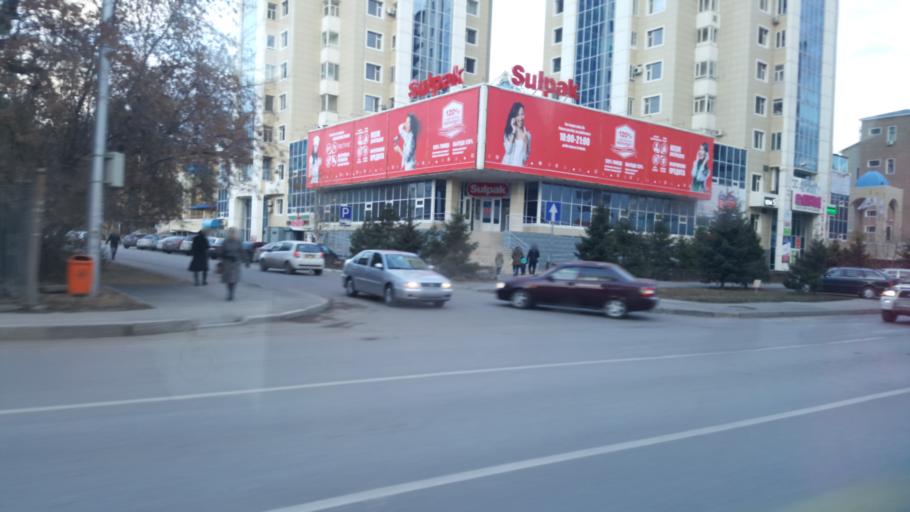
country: KZ
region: Astana Qalasy
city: Astana
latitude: 51.1664
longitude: 71.4341
